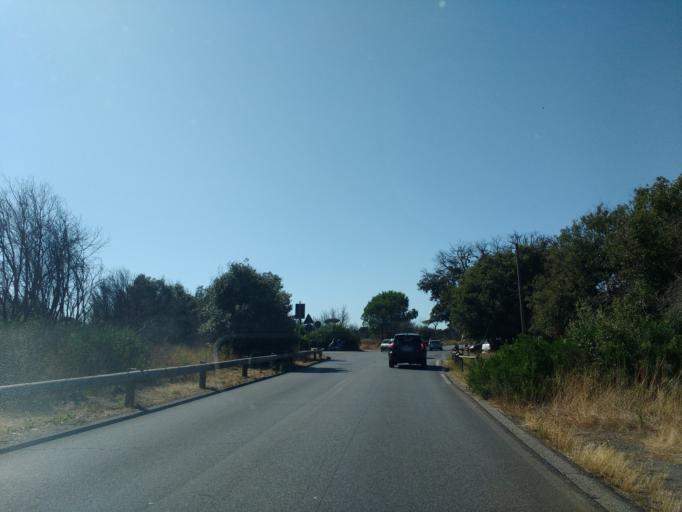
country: IT
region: Latium
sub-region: Citta metropolitana di Roma Capitale
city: Acilia-Castel Fusano-Ostia Antica
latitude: 41.7267
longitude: 12.3404
